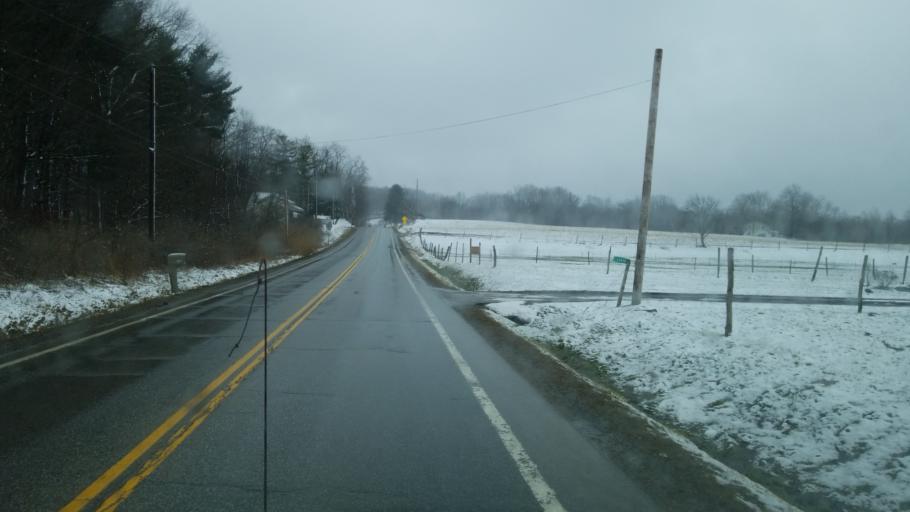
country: US
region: Ohio
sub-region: Geauga County
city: Middlefield
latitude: 41.3854
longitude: -81.0801
